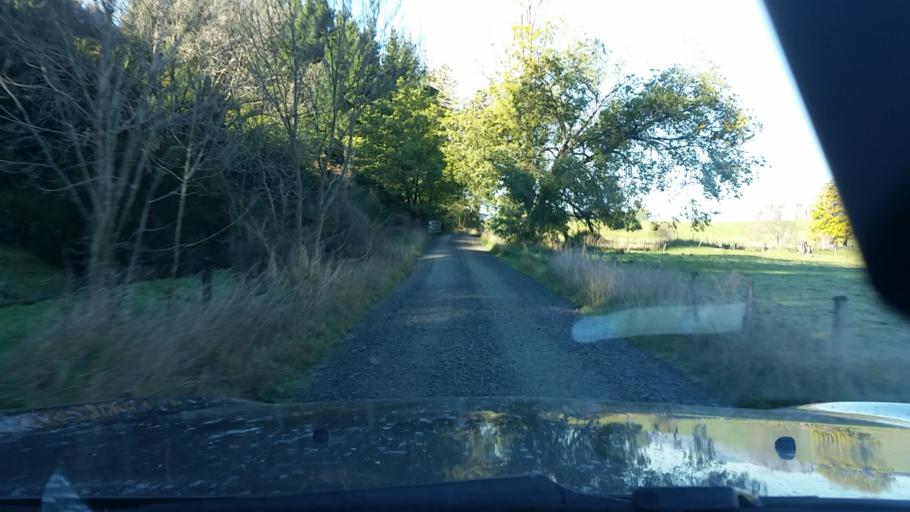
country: NZ
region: Marlborough
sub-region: Marlborough District
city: Blenheim
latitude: -41.4622
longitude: 173.7905
